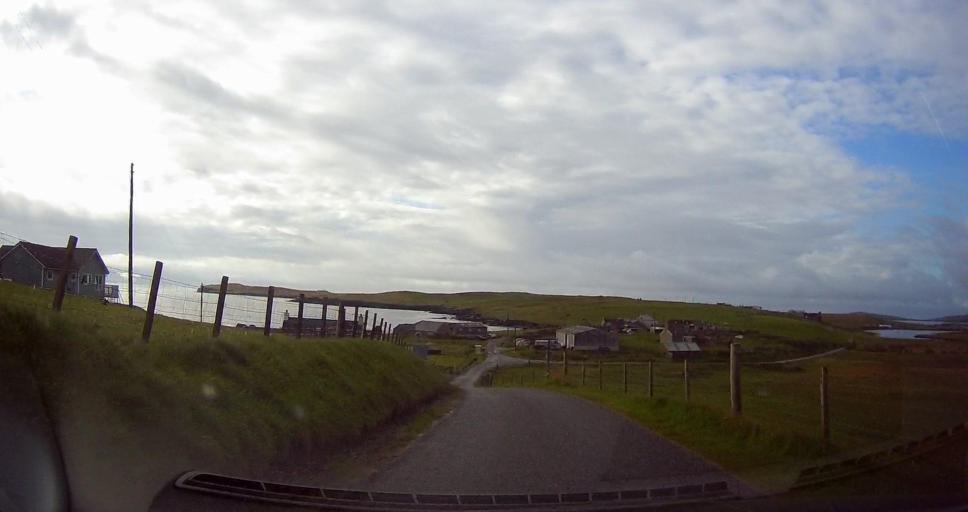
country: GB
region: Scotland
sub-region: Shetland Islands
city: Sandwick
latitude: 60.0513
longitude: -1.2071
